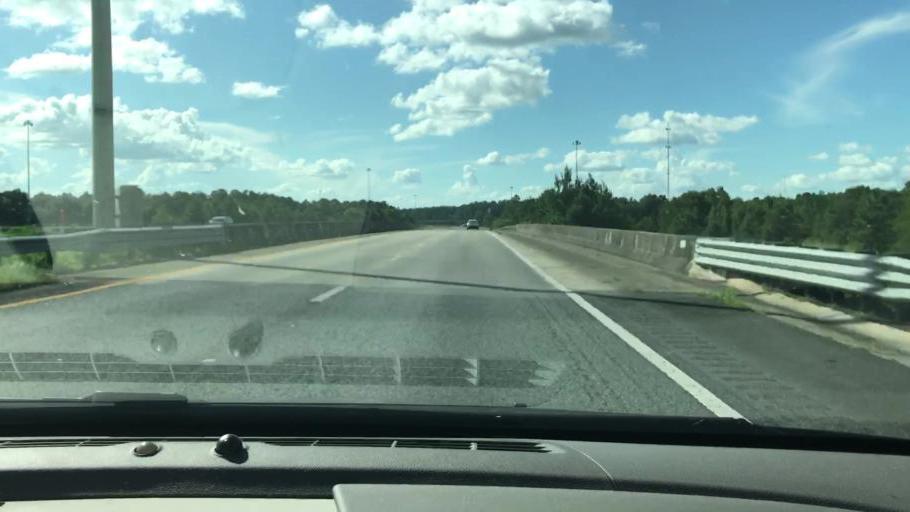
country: US
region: Florida
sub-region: Jackson County
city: Marianna
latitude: 30.7541
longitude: -85.2735
